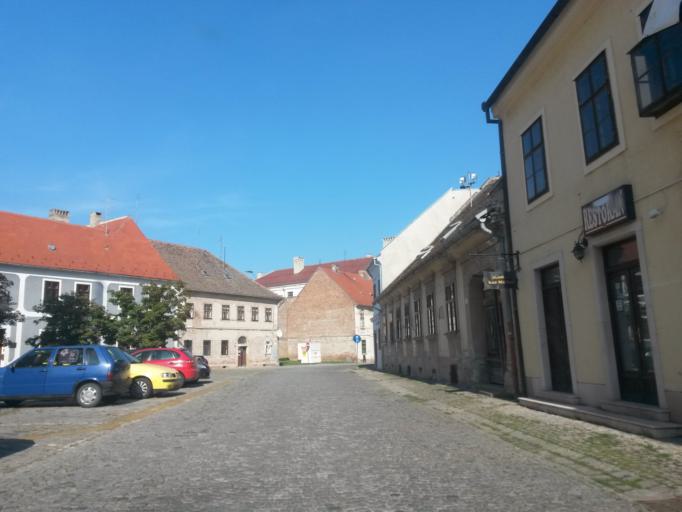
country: HR
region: Osjecko-Baranjska
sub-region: Grad Osijek
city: Osijek
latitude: 45.5608
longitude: 18.6942
